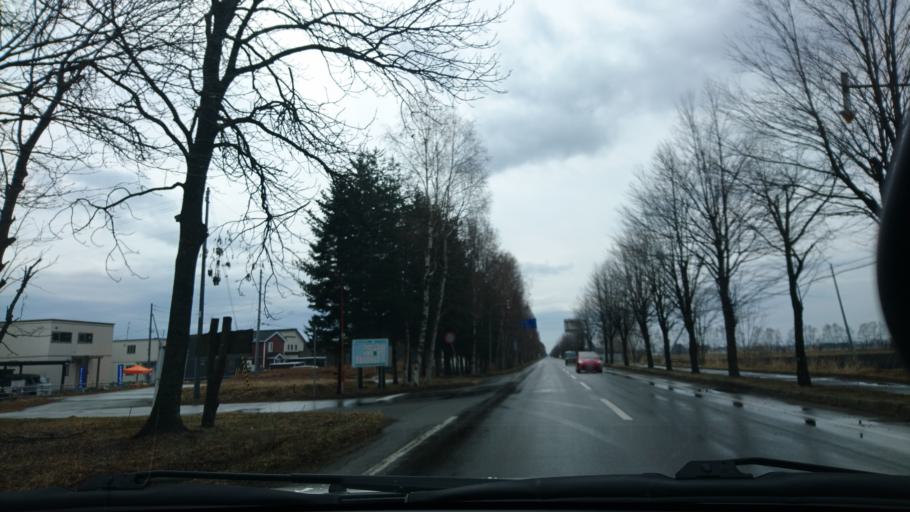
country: JP
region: Hokkaido
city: Otofuke
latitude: 43.0043
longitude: 143.1876
